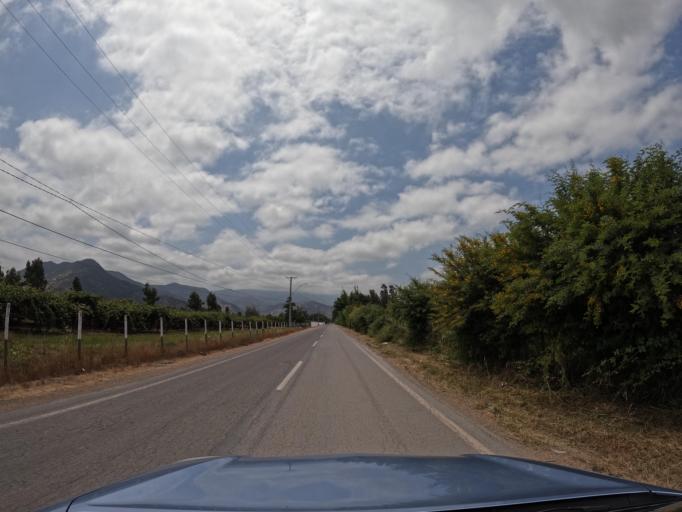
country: CL
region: O'Higgins
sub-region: Provincia de Colchagua
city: Chimbarongo
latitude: -34.7434
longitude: -70.9697
